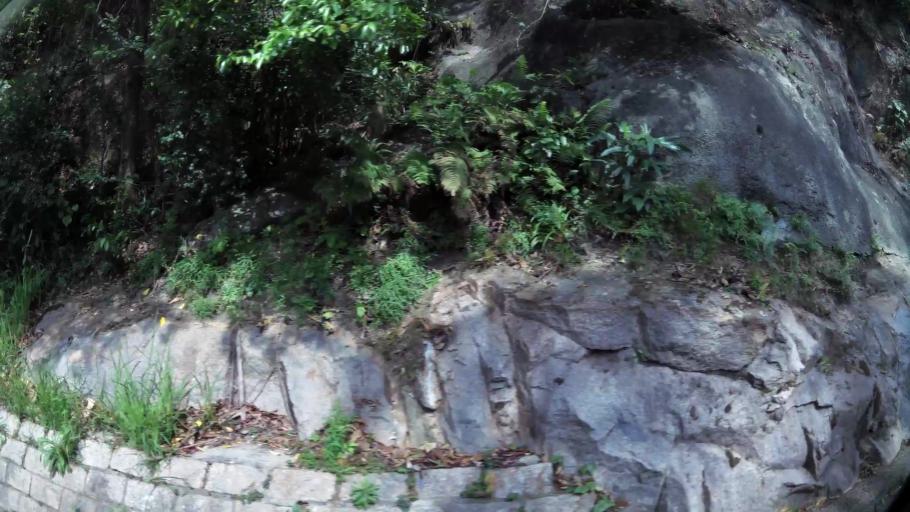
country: HK
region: Wanchai
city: Wan Chai
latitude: 22.2729
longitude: 114.1919
